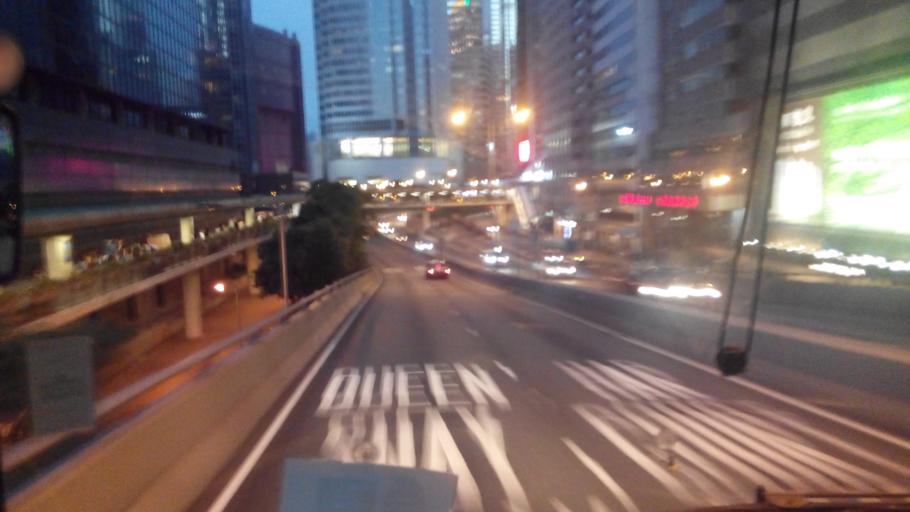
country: HK
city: Hong Kong
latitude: 22.2869
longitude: 114.1543
